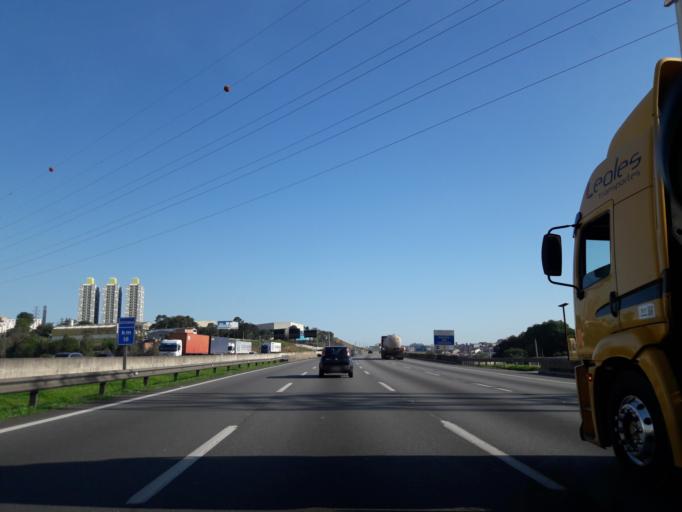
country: BR
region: Sao Paulo
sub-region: Carapicuiba
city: Carapicuiba
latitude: -23.5392
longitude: -46.8182
